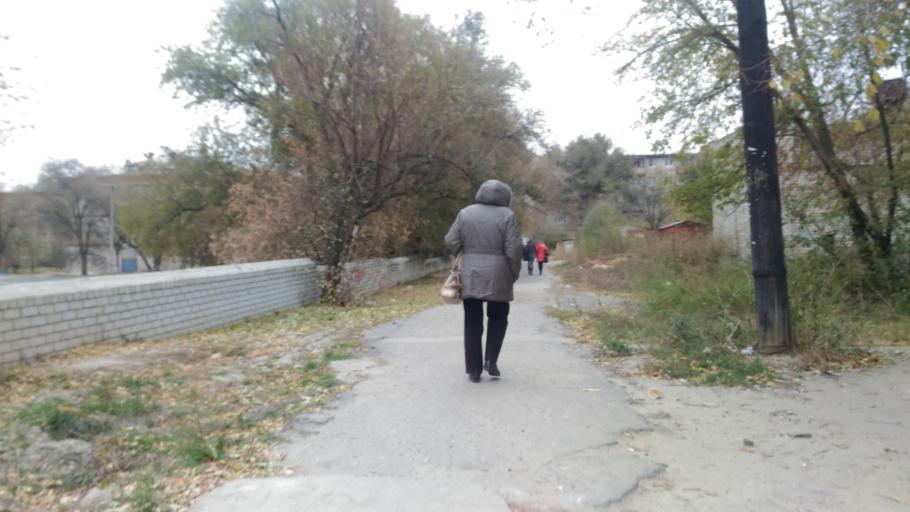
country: RU
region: Volgograd
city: Volgograd
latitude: 48.6491
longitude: 44.4314
